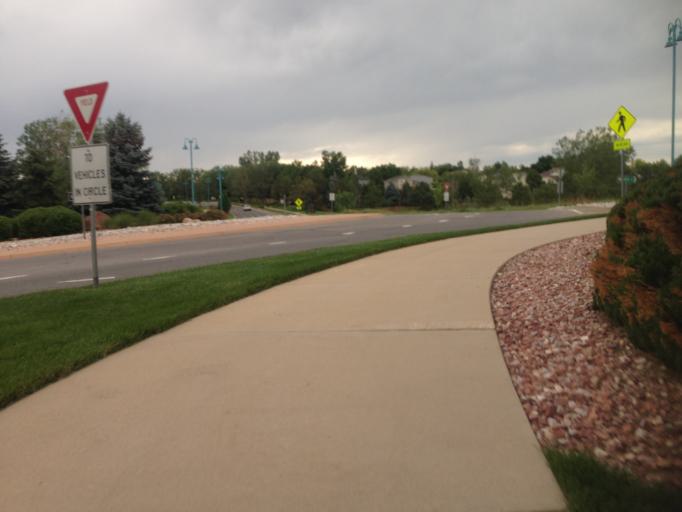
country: US
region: Colorado
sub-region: Boulder County
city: Superior
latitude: 39.9375
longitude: -105.1473
